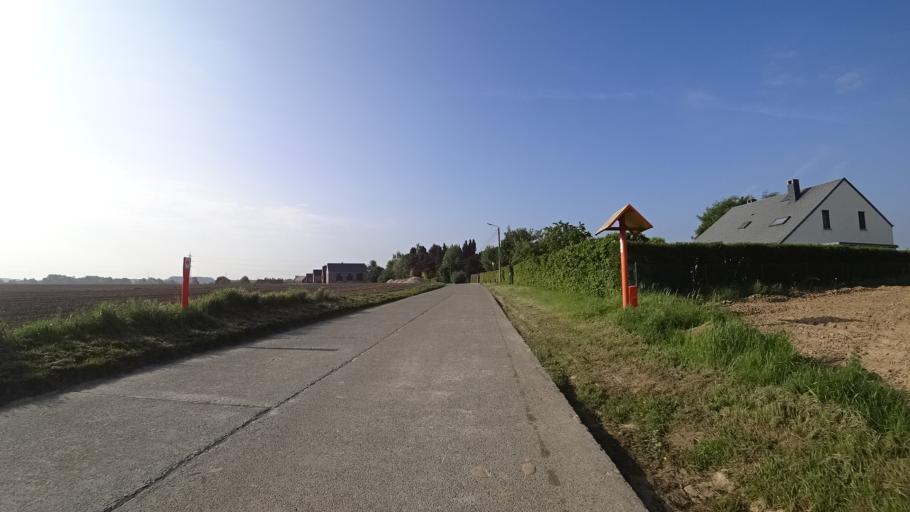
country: BE
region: Wallonia
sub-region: Province de Namur
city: Namur
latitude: 50.5234
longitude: 4.8241
